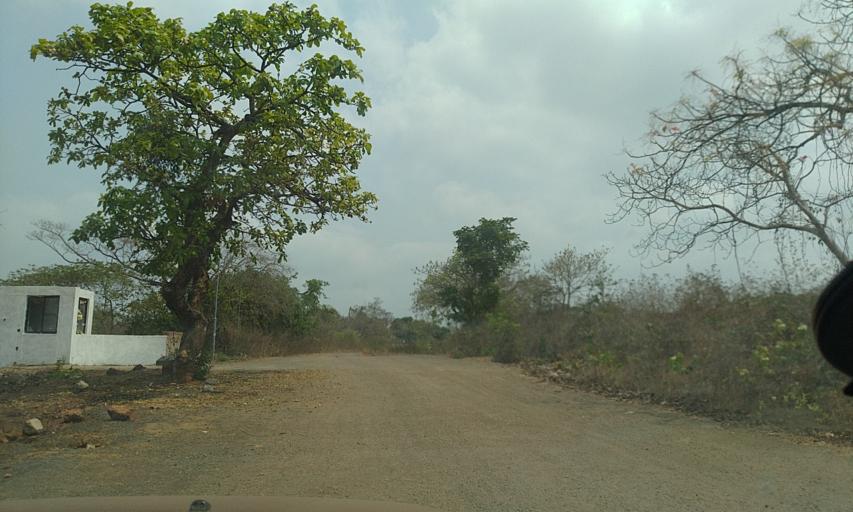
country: IN
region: Goa
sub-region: North Goa
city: Goa Velha
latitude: 15.4785
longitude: 73.9100
